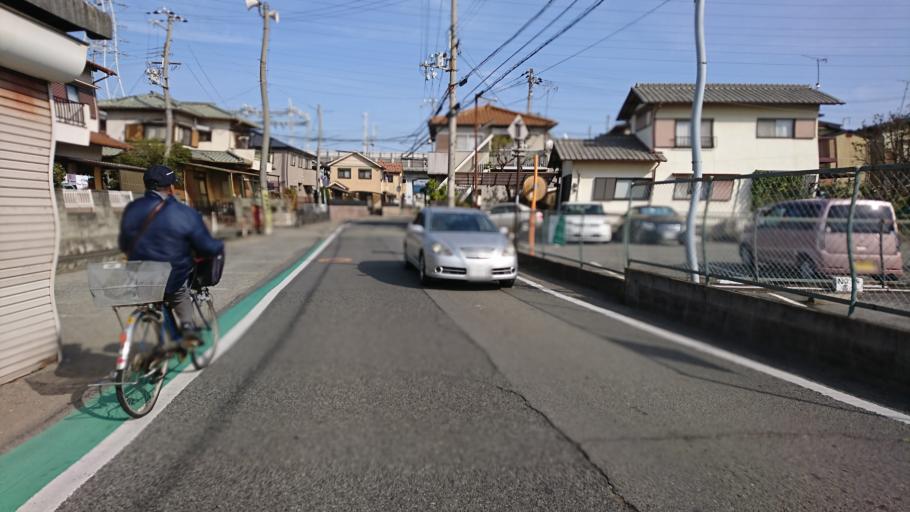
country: JP
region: Hyogo
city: Kakogawacho-honmachi
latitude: 34.7462
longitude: 134.8263
